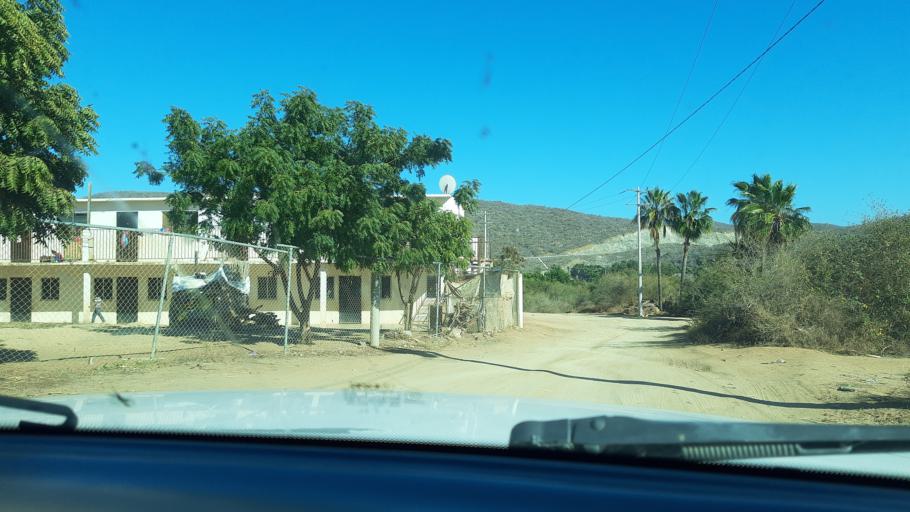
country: MX
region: Baja California Sur
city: Todos Santos
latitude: 23.4740
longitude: -110.2169
